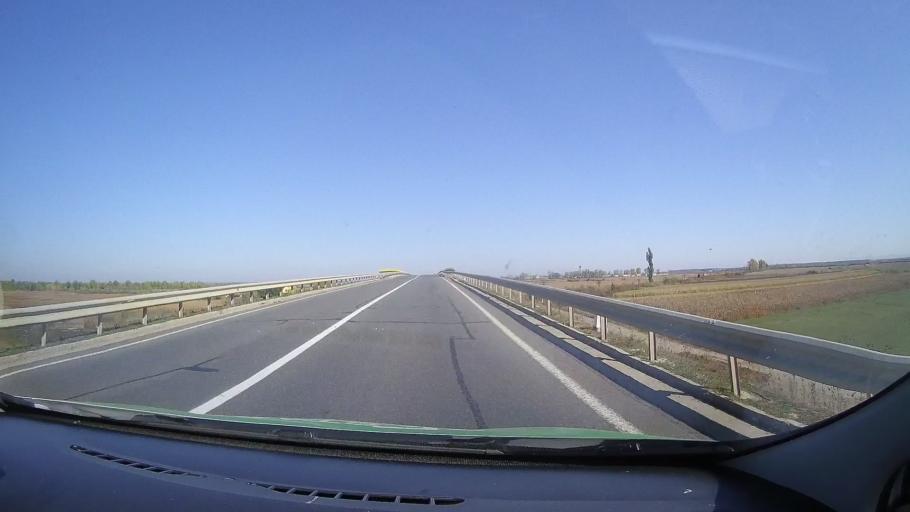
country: RO
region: Satu Mare
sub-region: Comuna Moftinu
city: Moftinu Mic
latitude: 47.6960
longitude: 22.6206
